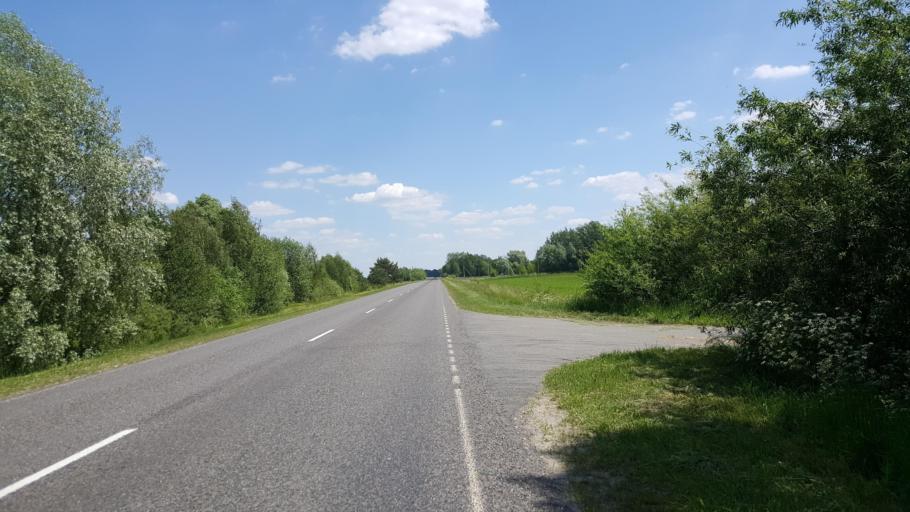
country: BY
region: Brest
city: Kobryn
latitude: 52.2025
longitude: 24.2062
